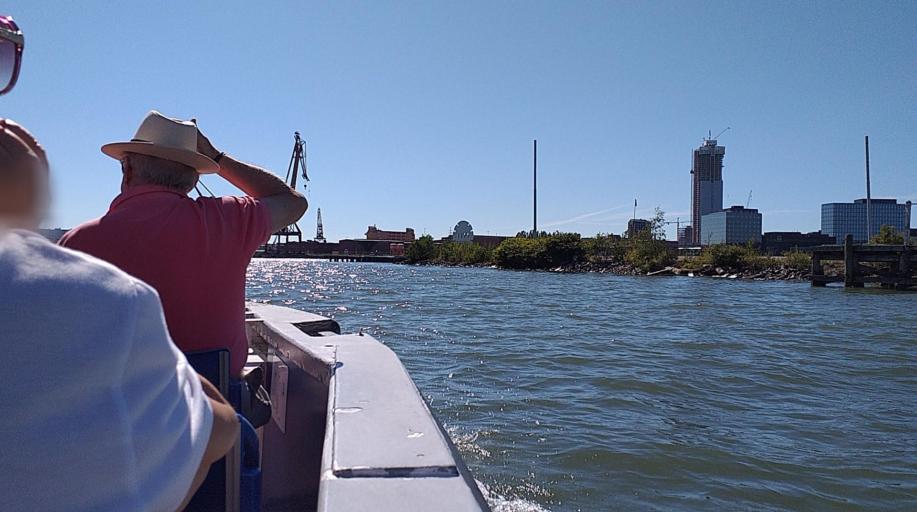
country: SE
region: Vaestra Goetaland
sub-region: Goteborg
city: Goeteborg
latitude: 57.7112
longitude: 11.9597
